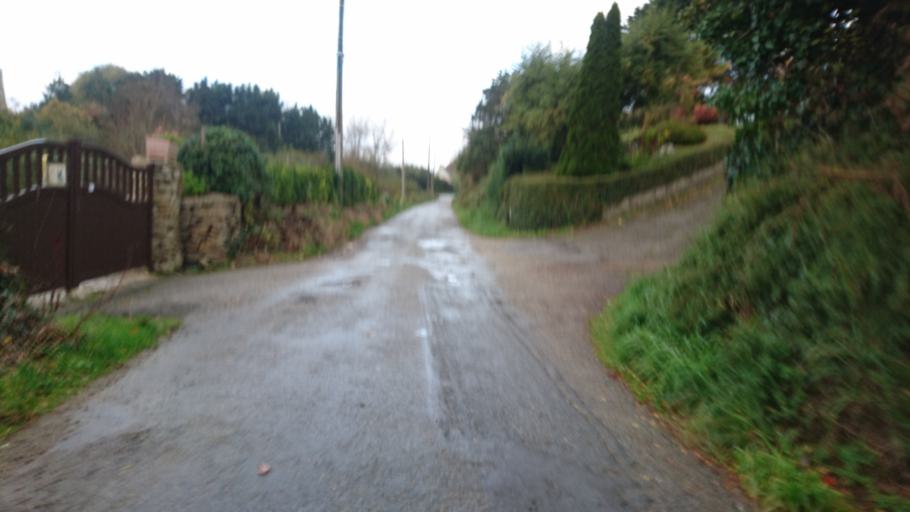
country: FR
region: Brittany
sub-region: Departement du Finistere
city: Lampaul-Plouarzel
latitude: 48.4427
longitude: -4.7683
